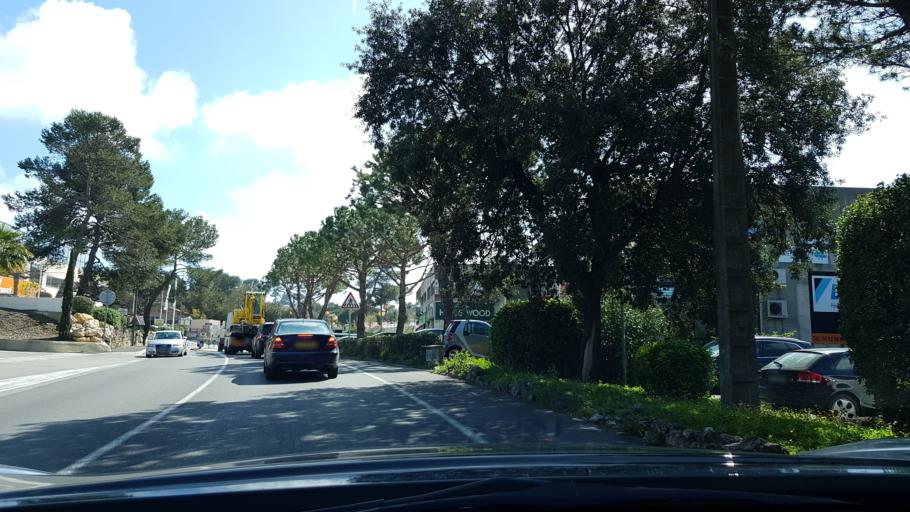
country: FR
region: Provence-Alpes-Cote d'Azur
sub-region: Departement des Alpes-Maritimes
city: Vallauris
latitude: 43.5924
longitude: 7.0562
